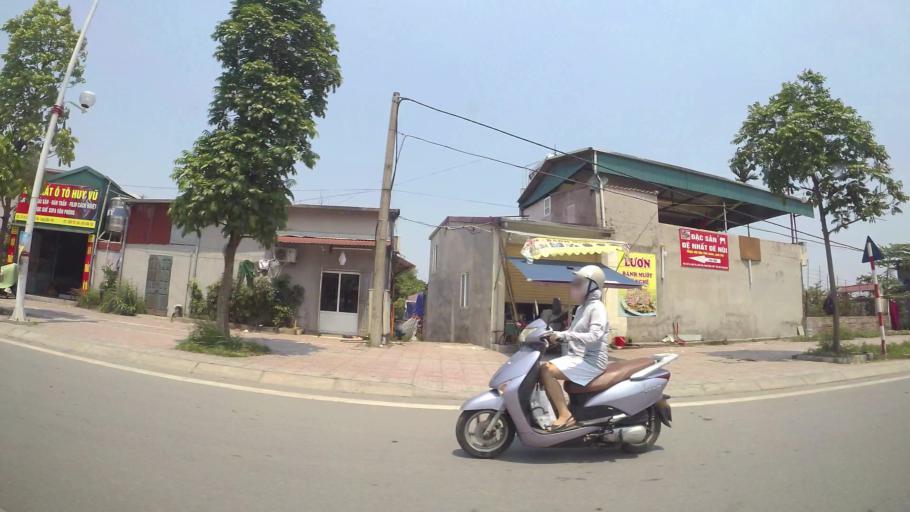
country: VN
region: Ha Noi
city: Hoan Kiem
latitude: 21.0350
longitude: 105.8800
